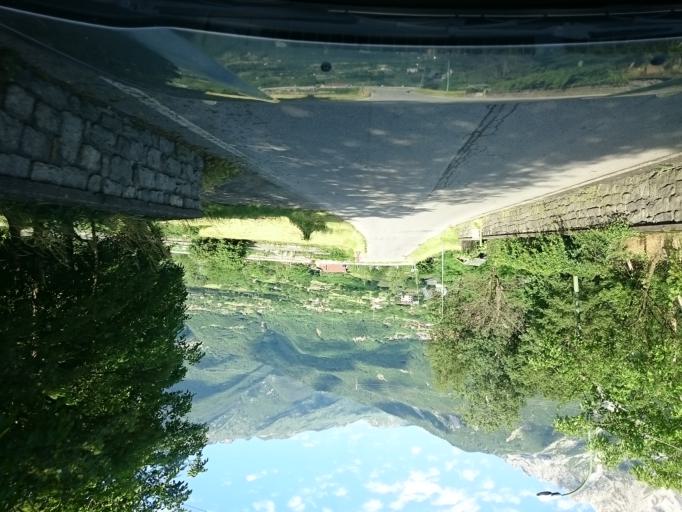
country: IT
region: Lombardy
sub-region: Provincia di Brescia
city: Ceto
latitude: 46.0115
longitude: 10.3502
